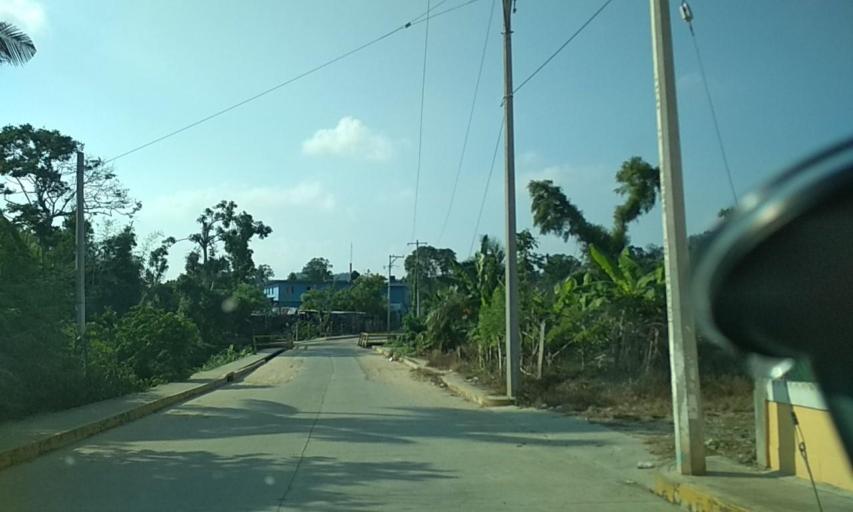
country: MX
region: Veracruz
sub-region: Papantla
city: Polutla
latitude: 20.5992
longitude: -97.2579
